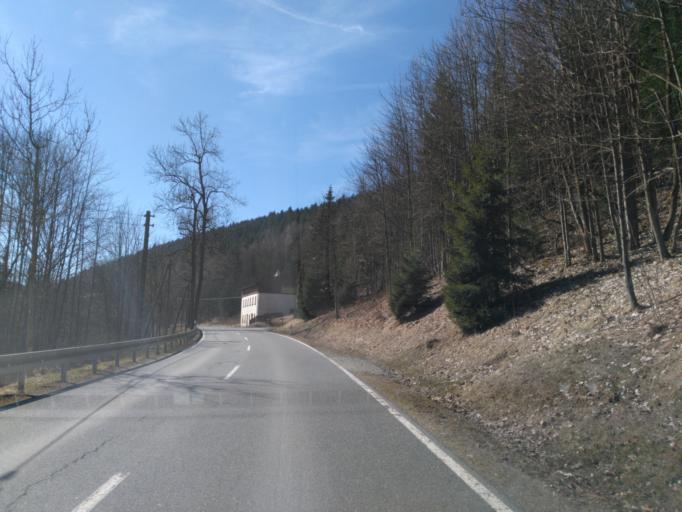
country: CZ
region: Ustecky
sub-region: Okres Chomutov
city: Vejprty
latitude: 50.4614
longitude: 13.0186
